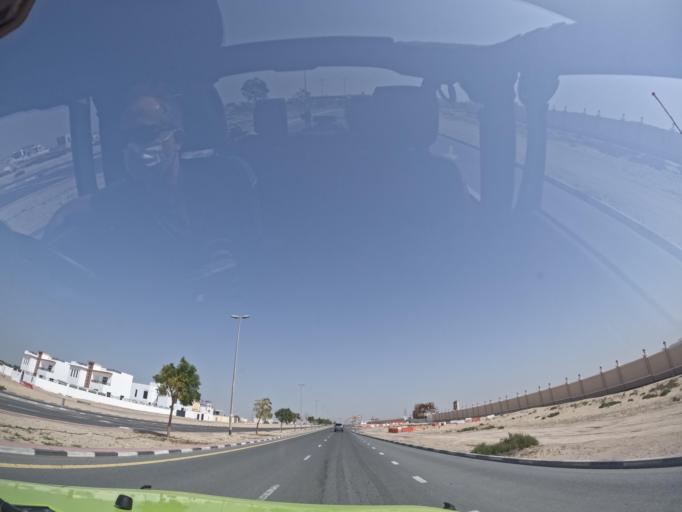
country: AE
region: Ash Shariqah
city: Sharjah
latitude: 25.1530
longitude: 55.3622
